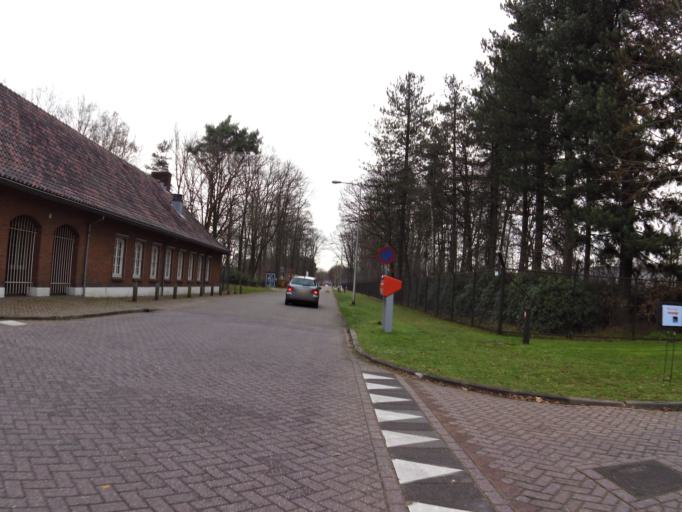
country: NL
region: North Brabant
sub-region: Gemeente Vught
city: Vught
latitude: 51.6592
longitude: 5.2597
